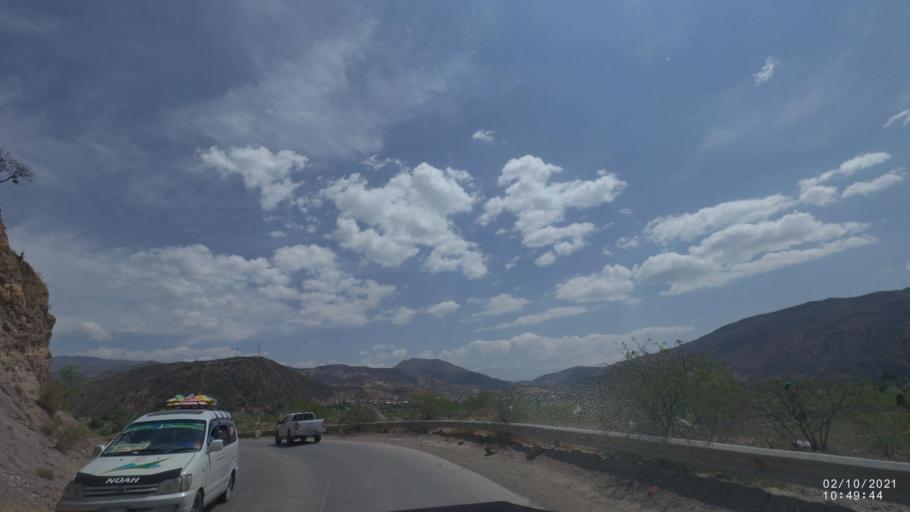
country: BO
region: Cochabamba
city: Sipe Sipe
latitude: -17.5780
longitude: -66.3460
